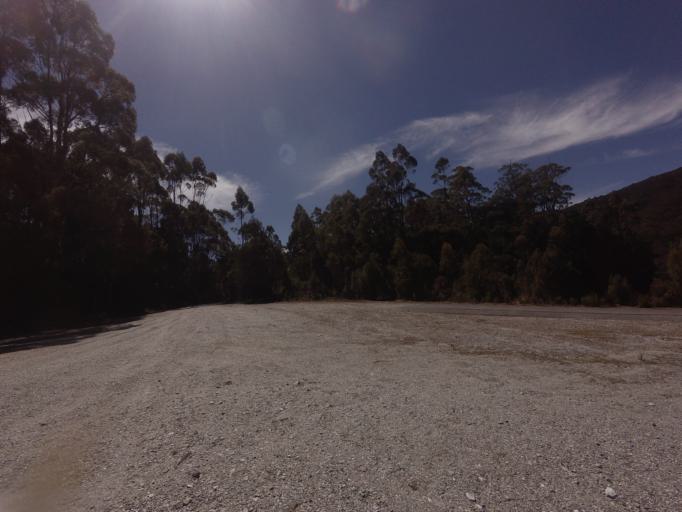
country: AU
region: Tasmania
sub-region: West Coast
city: Queenstown
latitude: -42.7689
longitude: 145.9865
